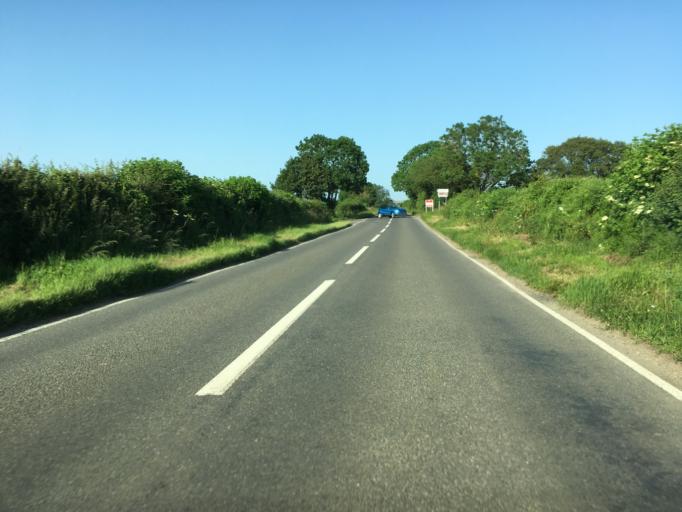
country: GB
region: England
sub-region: Oxfordshire
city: Shipton under Wychwood
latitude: 51.8599
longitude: -1.5560
